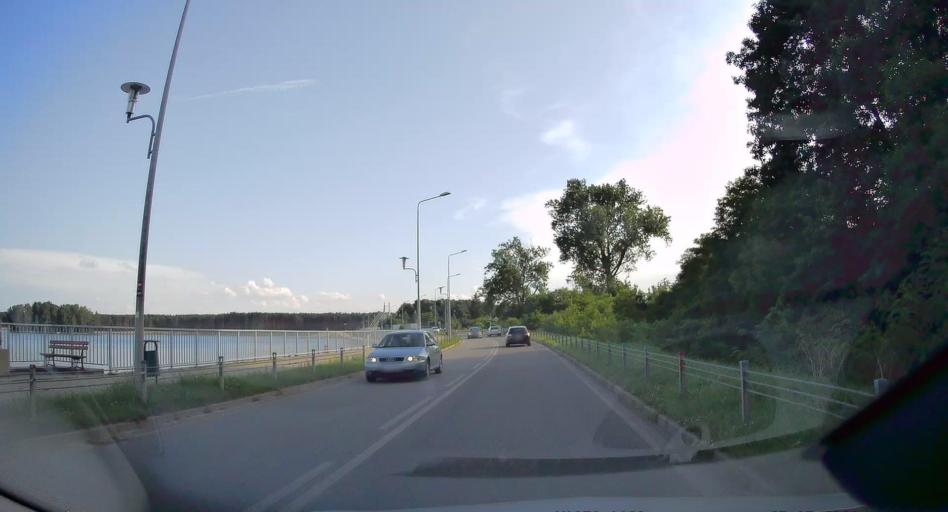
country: PL
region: Swietokrzyskie
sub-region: Powiat konecki
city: Smykow
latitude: 51.1153
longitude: 20.3500
